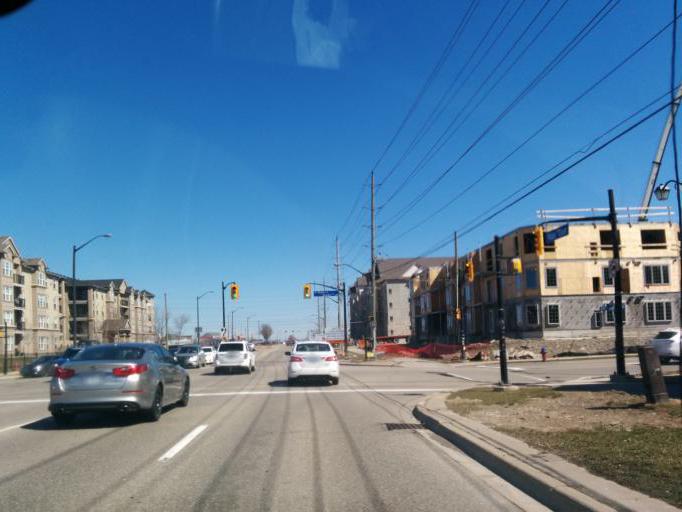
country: CA
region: Ontario
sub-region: Halton
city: Milton
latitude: 43.5355
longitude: -79.8587
